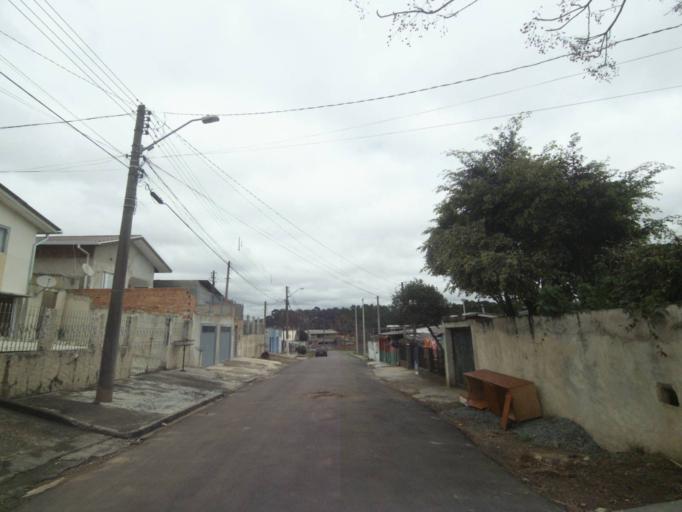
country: BR
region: Parana
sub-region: Sao Jose Dos Pinhais
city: Sao Jose dos Pinhais
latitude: -25.5372
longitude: -49.2995
